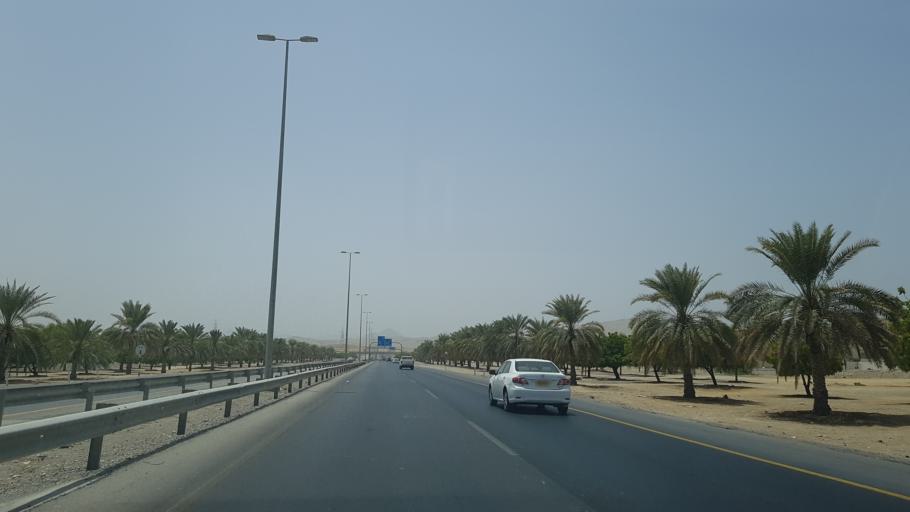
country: OM
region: Muhafazat Masqat
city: As Sib al Jadidah
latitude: 23.5803
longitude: 58.1954
